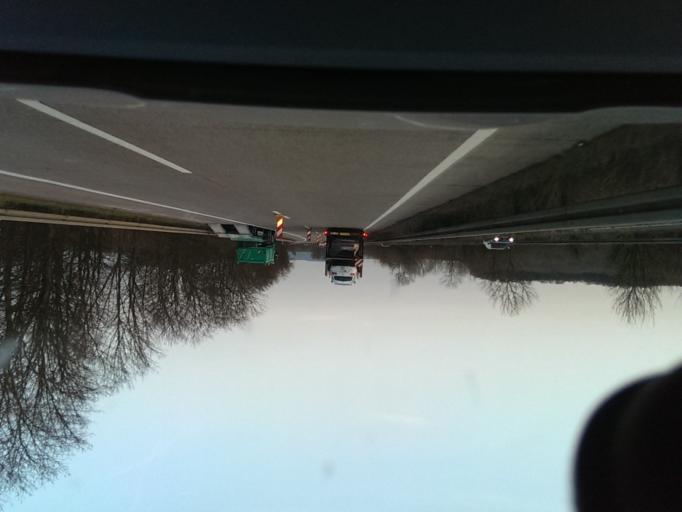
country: DE
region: Lower Saxony
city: Kalefeld
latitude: 51.7590
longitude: 10.0142
